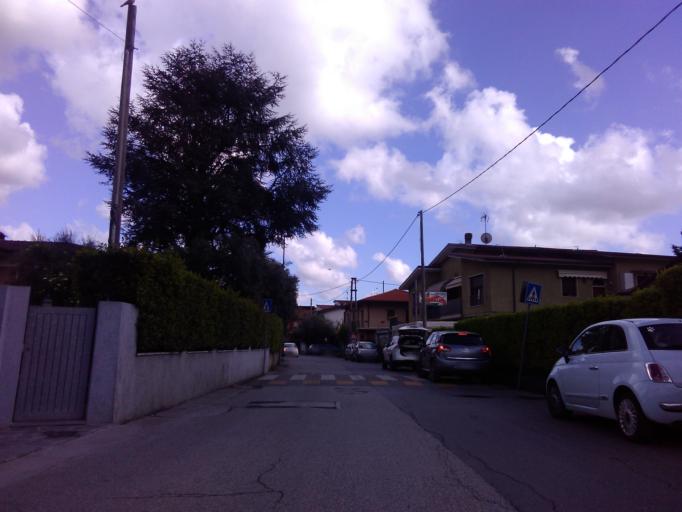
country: IT
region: Tuscany
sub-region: Provincia di Lucca
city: Ripa-Pozzi-Querceta-Ponterosso
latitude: 43.9848
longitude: 10.2091
